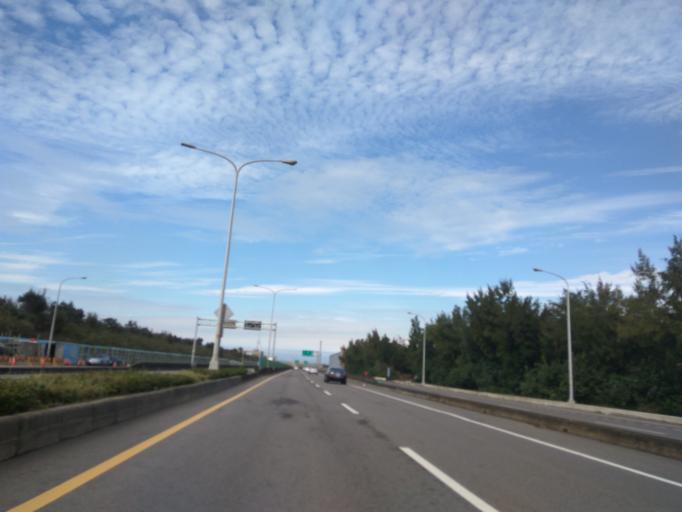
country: TW
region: Taiwan
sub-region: Hsinchu
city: Zhubei
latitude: 25.0259
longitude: 121.0609
